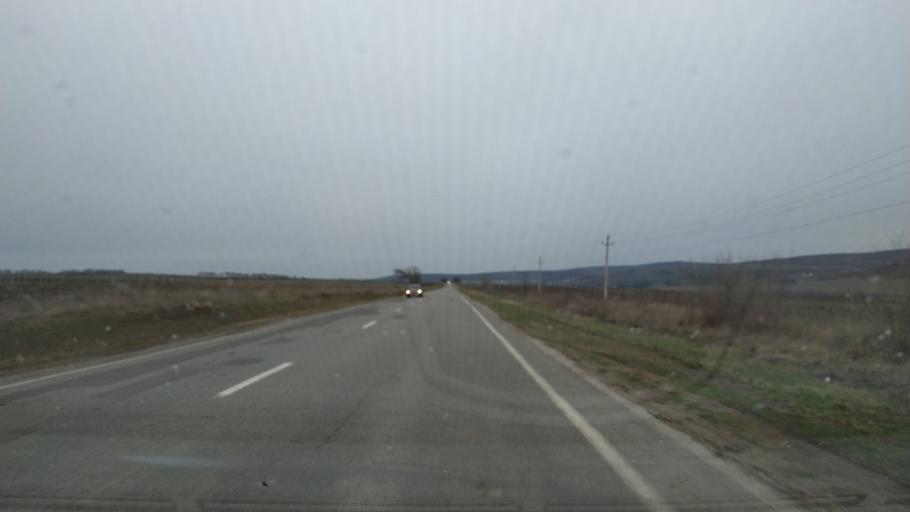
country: MD
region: Hincesti
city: Hincesti
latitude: 46.7604
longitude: 28.5226
